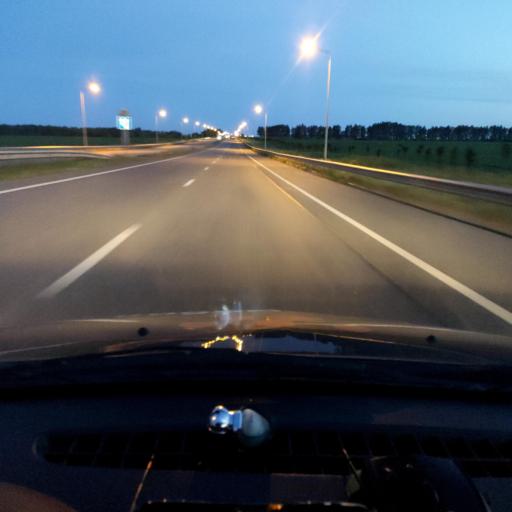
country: RU
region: Belgorod
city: Gubkin
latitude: 51.2382
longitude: 37.5146
